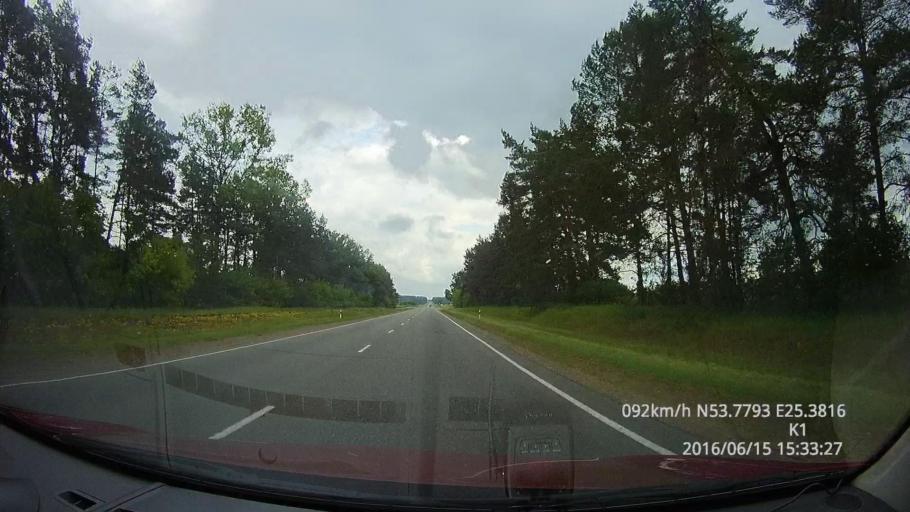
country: BY
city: Berezovka
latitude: 53.7786
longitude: 25.3820
